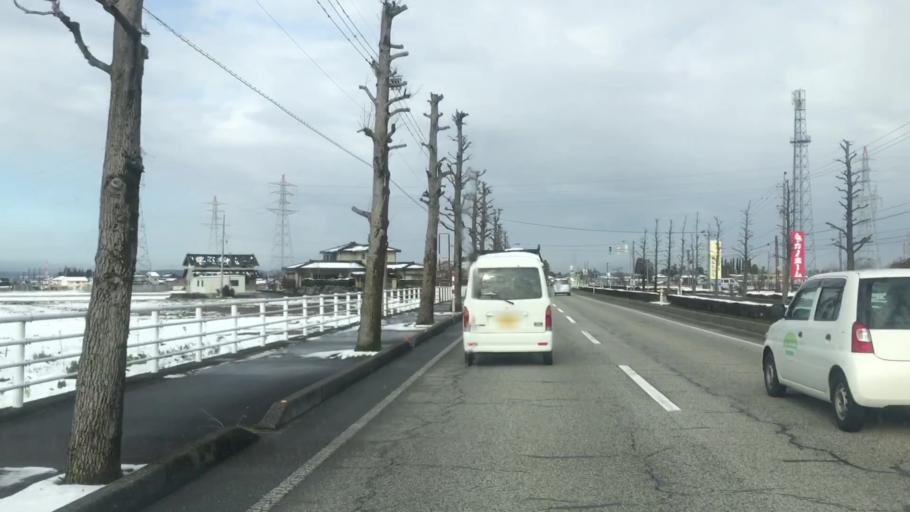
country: JP
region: Toyama
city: Toyama-shi
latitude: 36.6381
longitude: 137.2400
